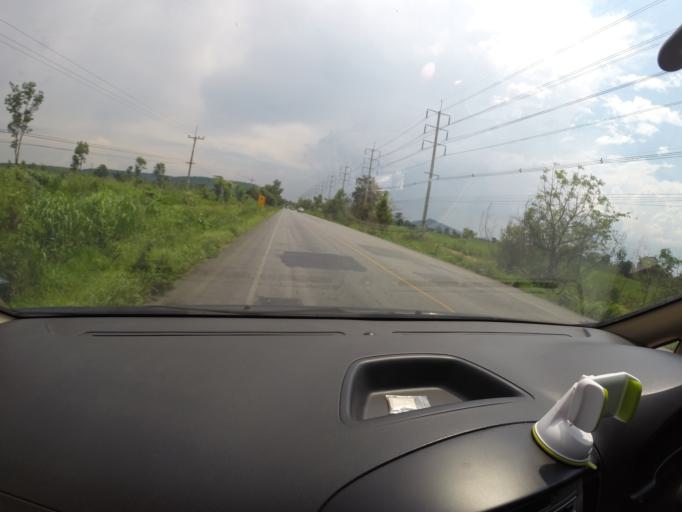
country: TH
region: Lop Buri
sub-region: Amphoe Lam Sonthi
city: Lam Sonthi
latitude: 15.1083
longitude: 101.4570
